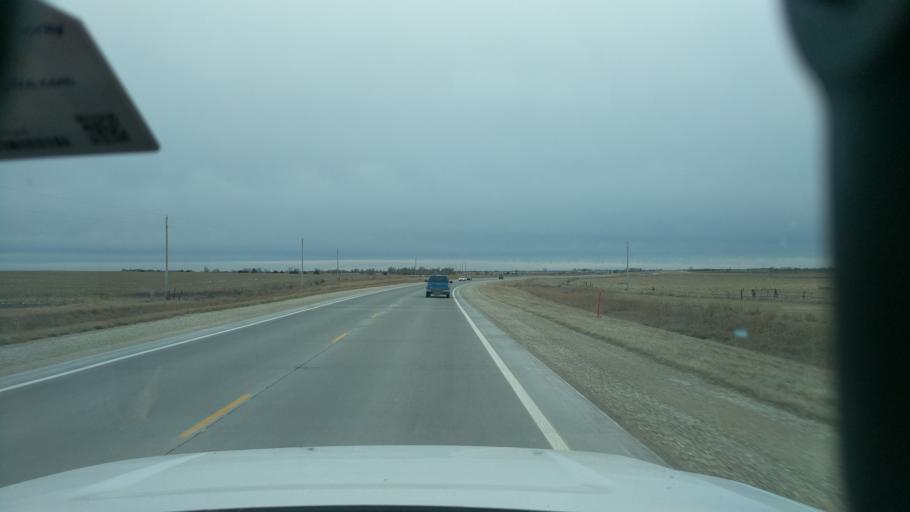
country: US
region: Kansas
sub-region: Dickinson County
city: Herington
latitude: 38.5741
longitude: -96.9483
